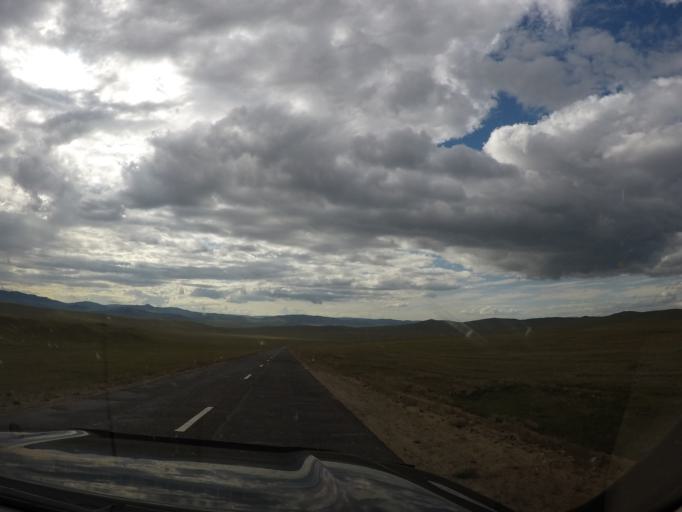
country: MN
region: Hentiy
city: Modot
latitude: 47.5904
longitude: 109.2691
